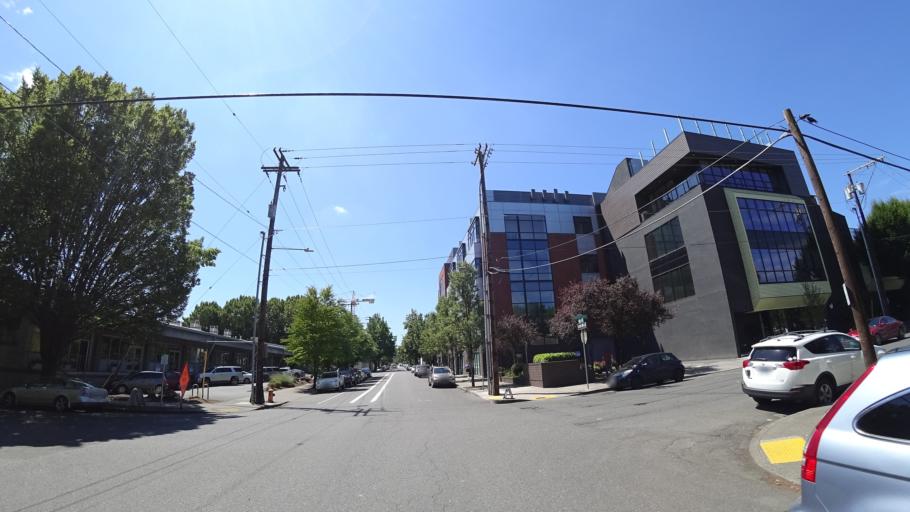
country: US
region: Oregon
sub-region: Multnomah County
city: Portland
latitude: 45.5343
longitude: -122.6897
